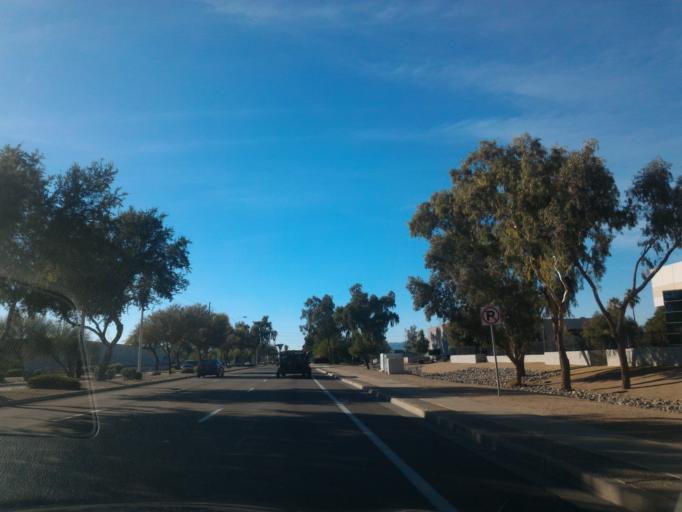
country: US
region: Arizona
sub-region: Maricopa County
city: Guadalupe
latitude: 33.3054
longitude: -111.9523
